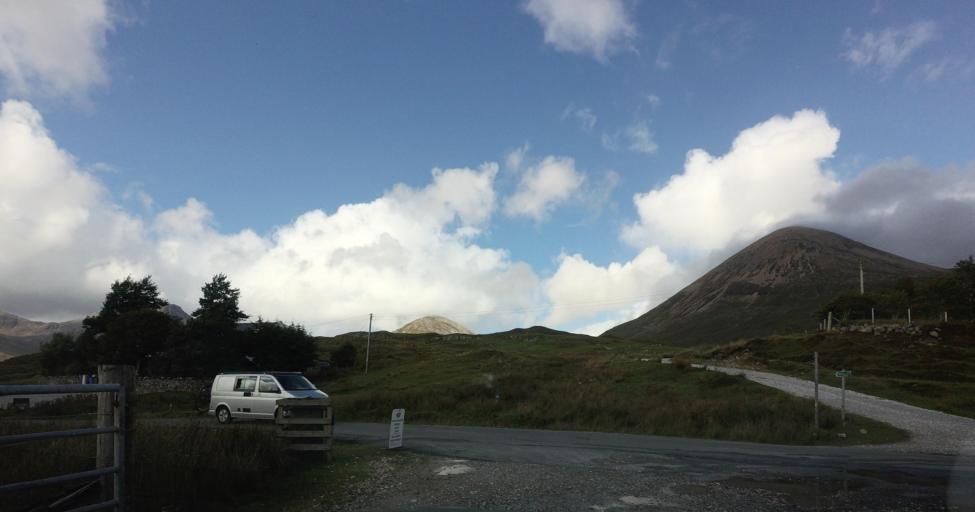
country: GB
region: Scotland
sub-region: Highland
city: Portree
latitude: 57.2158
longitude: -6.0171
